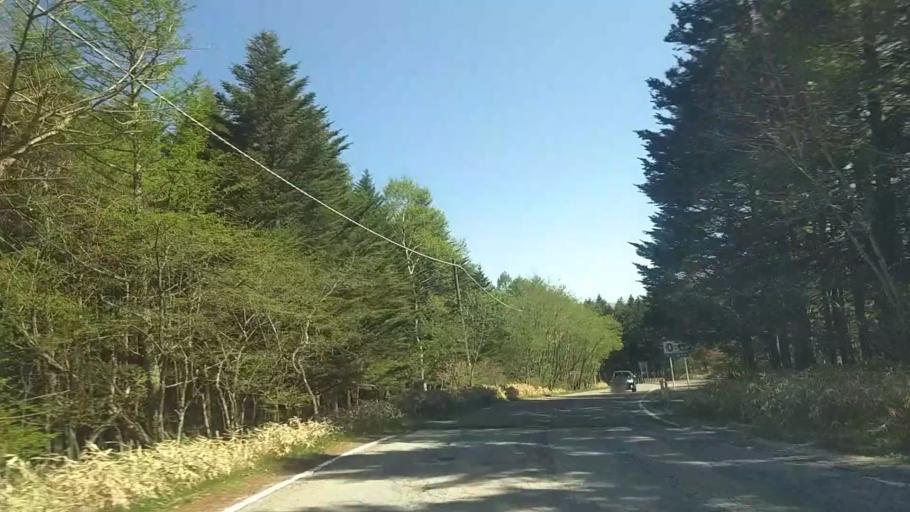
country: JP
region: Yamanashi
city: Nirasaki
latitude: 35.9440
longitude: 138.4197
